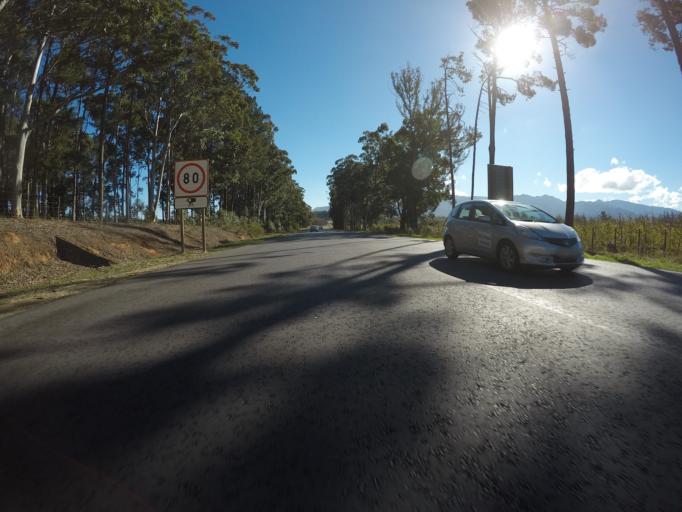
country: ZA
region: Western Cape
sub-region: Overberg District Municipality
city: Grabouw
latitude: -34.1686
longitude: 19.0428
